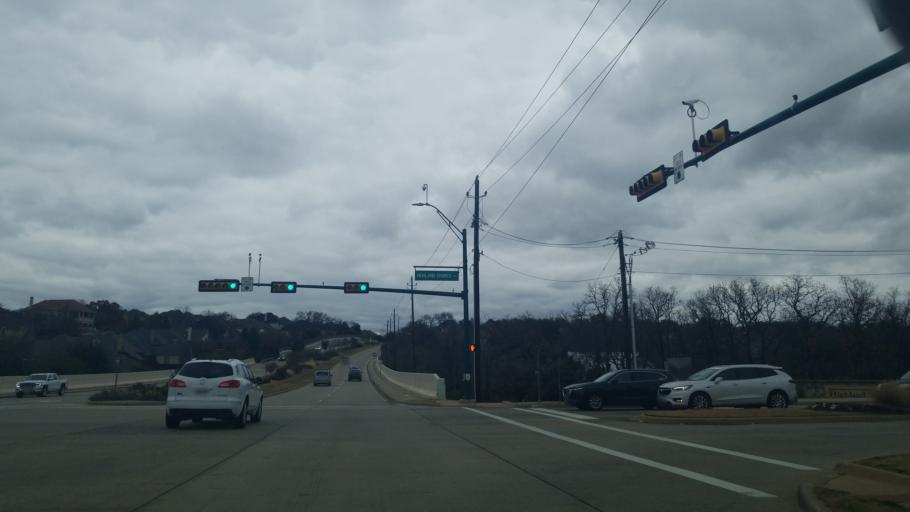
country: US
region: Texas
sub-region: Denton County
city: Copper Canyon
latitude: 33.0922
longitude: -97.0792
